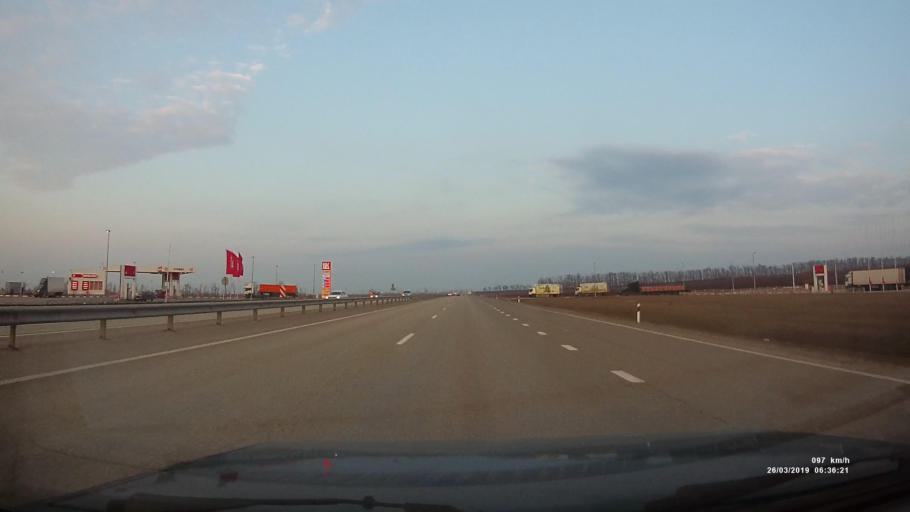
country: RU
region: Rostov
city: Chaltyr
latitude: 47.2834
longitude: 39.4259
